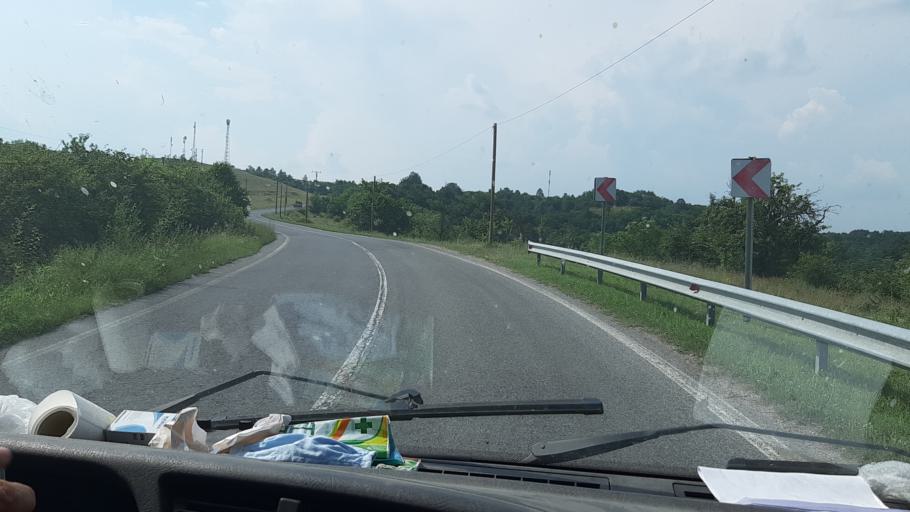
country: RO
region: Caras-Severin
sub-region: Comuna Farliug
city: Farliug
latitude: 45.5146
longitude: 21.8779
